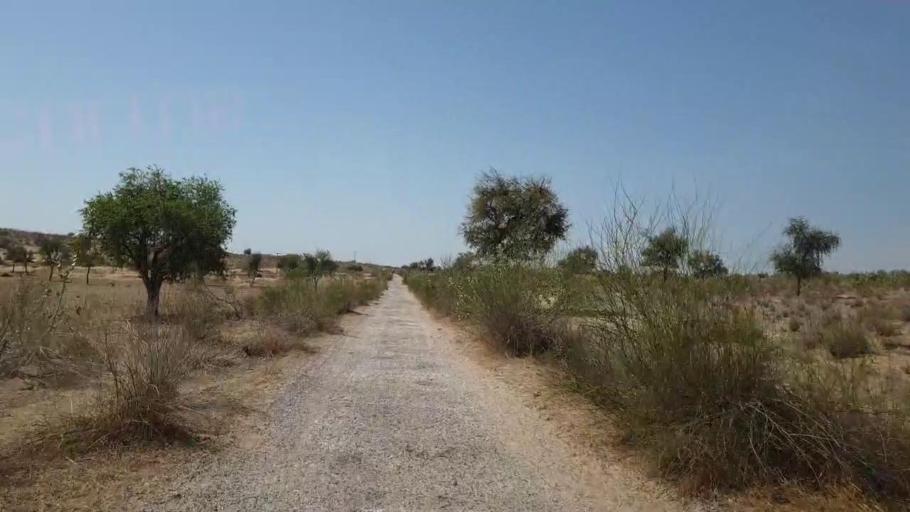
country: PK
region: Sindh
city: Umarkot
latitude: 25.1503
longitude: 69.9404
